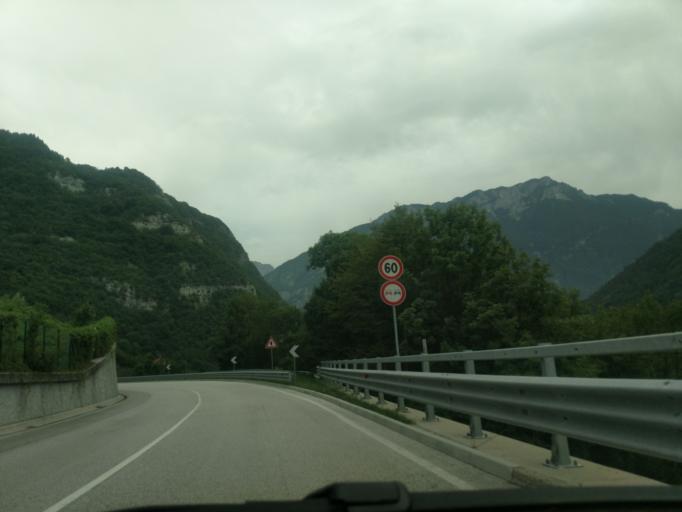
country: IT
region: Veneto
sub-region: Provincia di Belluno
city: Longarone
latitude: 46.2630
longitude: 12.2826
